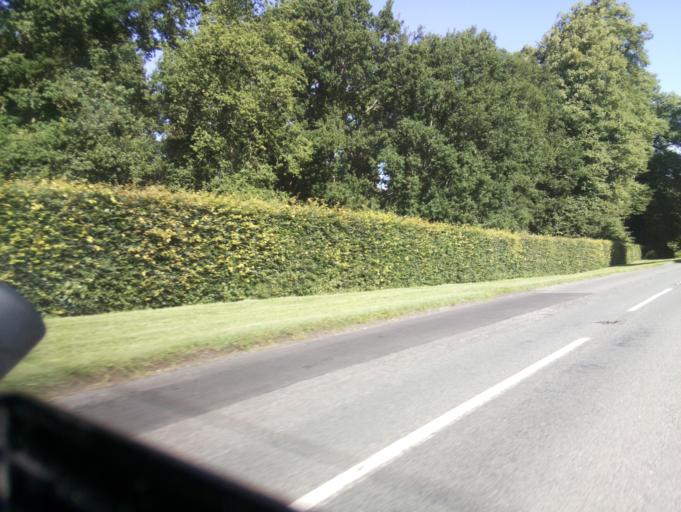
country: GB
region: England
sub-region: Herefordshire
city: Yatton
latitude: 51.9615
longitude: -2.5442
